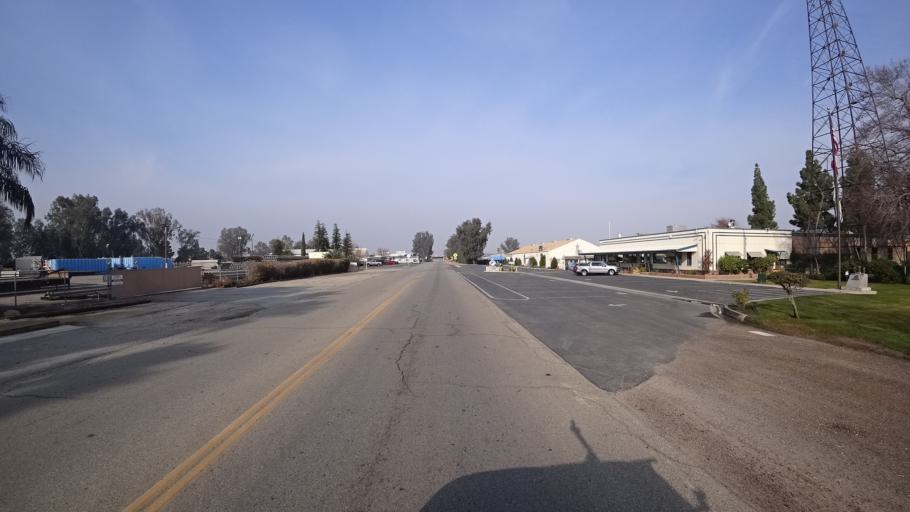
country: US
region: California
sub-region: Kern County
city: Oildale
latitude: 35.4050
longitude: -119.0440
